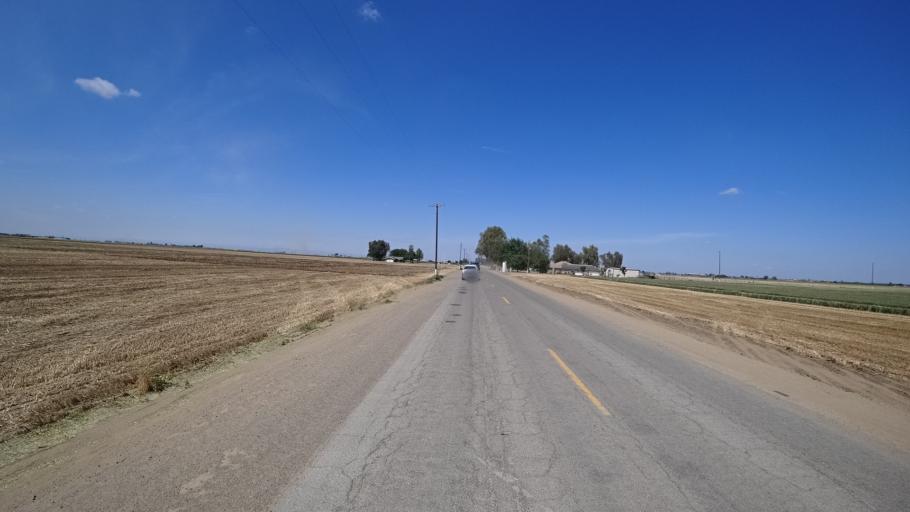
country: US
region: California
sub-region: Kings County
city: Home Garden
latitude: 36.2694
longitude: -119.6039
